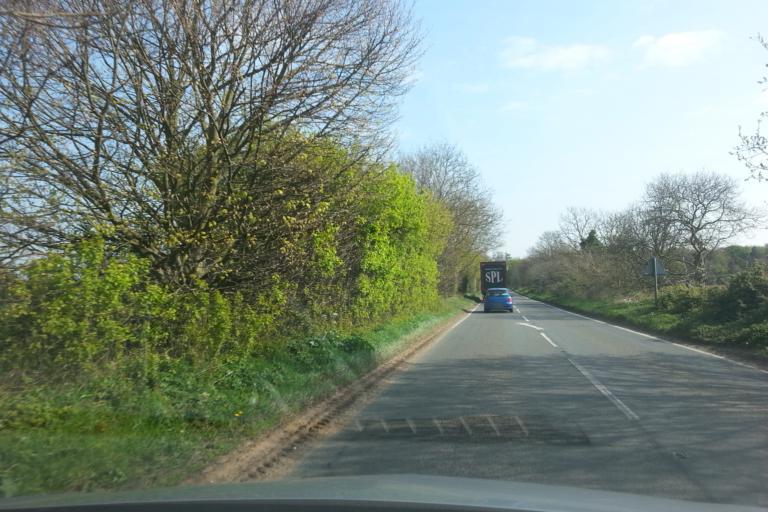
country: GB
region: England
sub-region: Suffolk
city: Wickham Market
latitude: 52.1191
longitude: 1.3874
